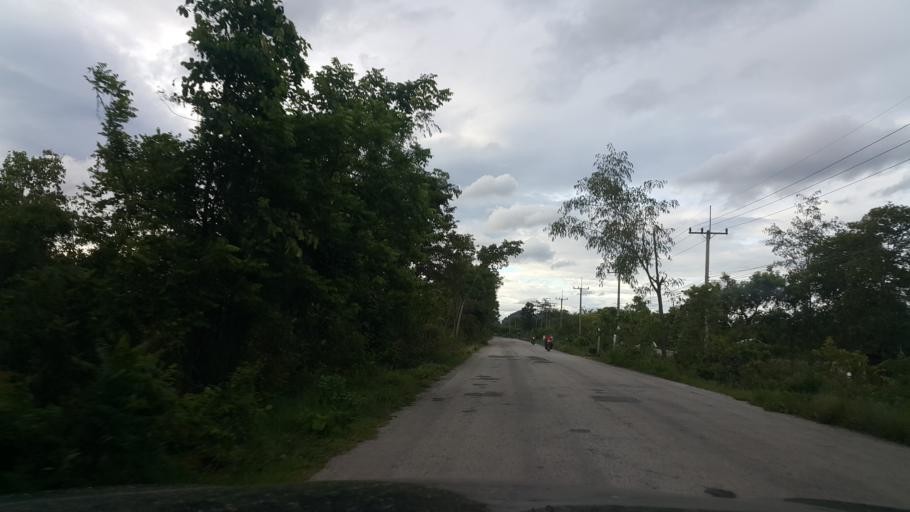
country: TH
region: Sukhothai
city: Thung Saliam
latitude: 17.1745
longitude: 99.5249
